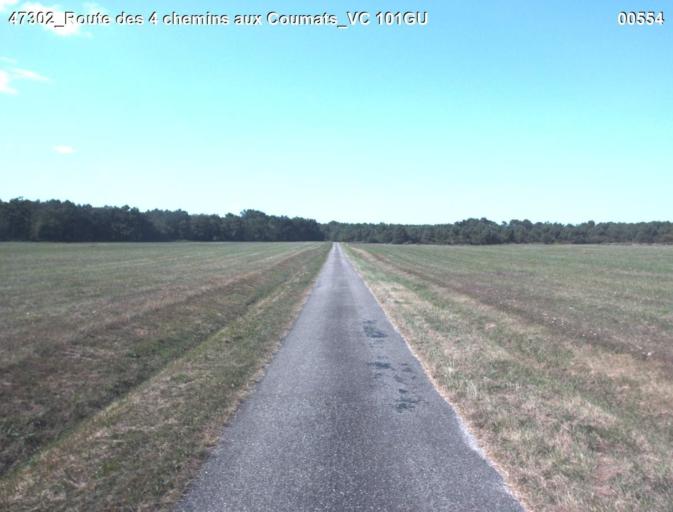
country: FR
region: Aquitaine
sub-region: Departement des Landes
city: Gabarret
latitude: 44.0175
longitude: 0.0875
